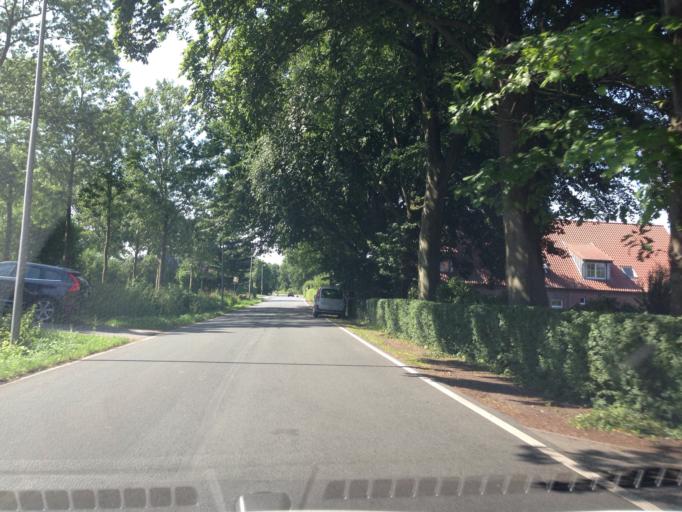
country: DE
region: North Rhine-Westphalia
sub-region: Regierungsbezirk Munster
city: Muenster
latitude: 51.9628
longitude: 7.5757
